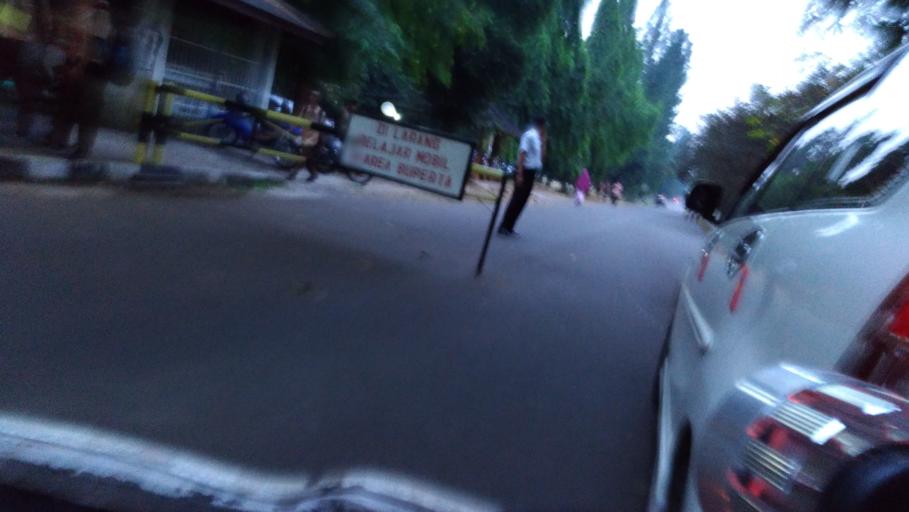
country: ID
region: West Java
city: Cileungsir
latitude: -6.3698
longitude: 106.8968
